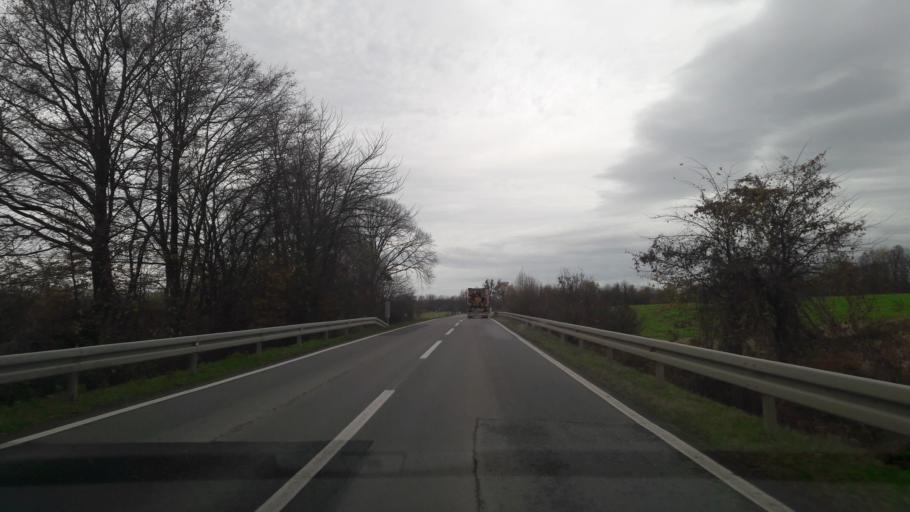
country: HR
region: Virovitick-Podravska
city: Orahovica
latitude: 45.5394
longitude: 17.9266
